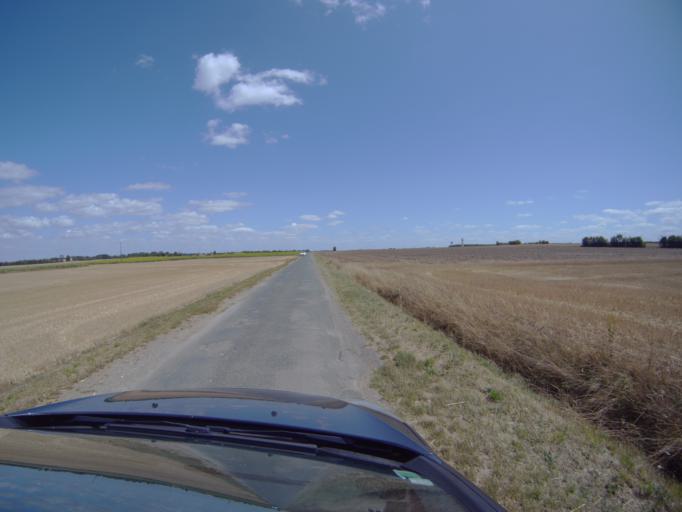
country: FR
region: Poitou-Charentes
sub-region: Departement de la Charente-Maritime
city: Courcon
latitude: 46.2475
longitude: -0.8025
